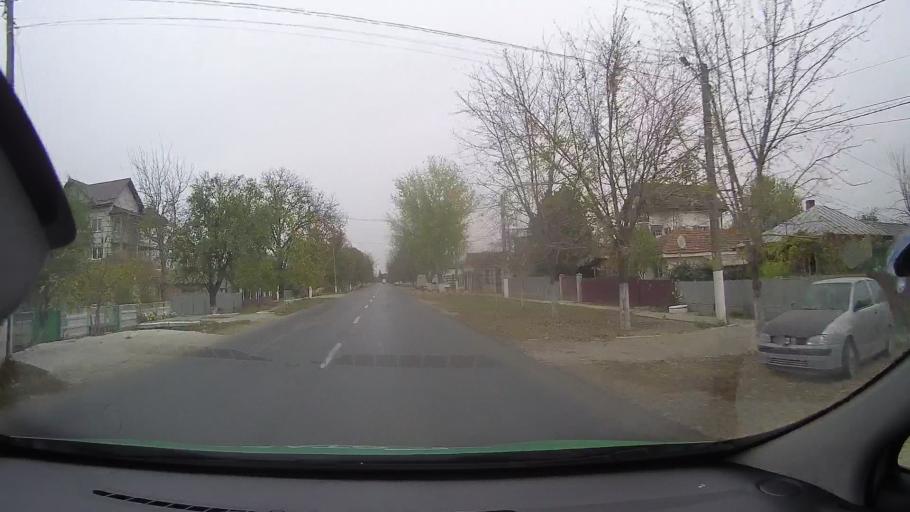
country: RO
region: Ialomita
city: Tandarei
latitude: 44.6492
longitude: 27.6553
